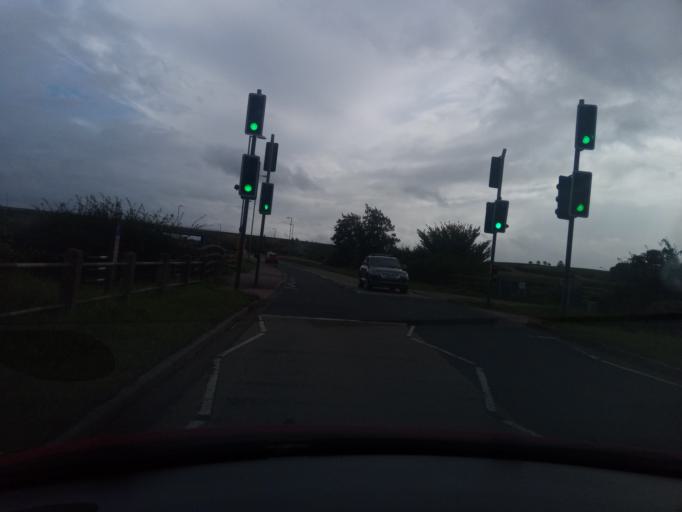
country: GB
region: England
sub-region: Nottinghamshire
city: Cotgrave
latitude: 52.9193
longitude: -1.0124
